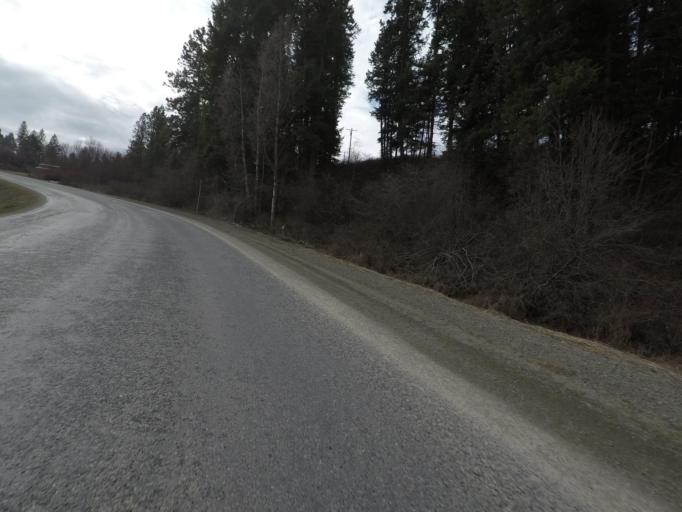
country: US
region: Washington
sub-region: Stevens County
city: Colville
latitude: 48.5116
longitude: -117.8683
